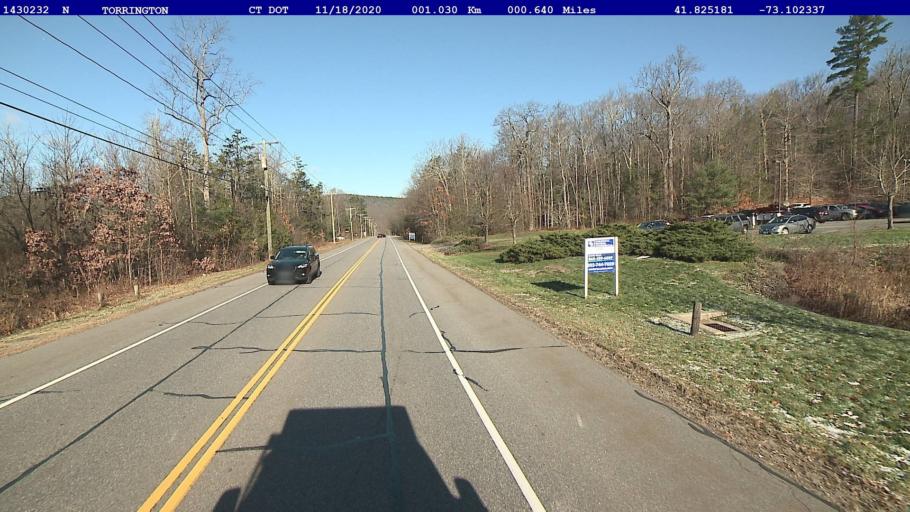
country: US
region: Connecticut
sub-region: Litchfield County
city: Torrington
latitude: 41.8252
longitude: -73.1023
